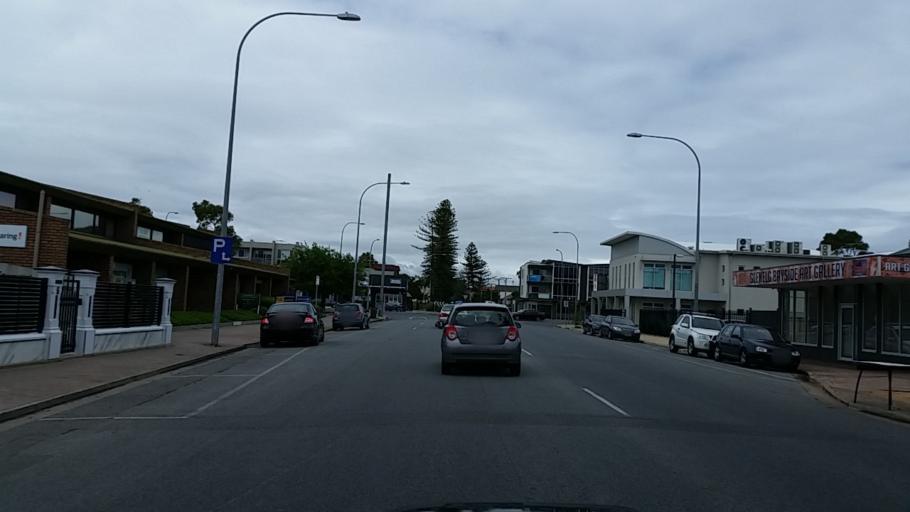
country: AU
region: South Australia
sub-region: Adelaide
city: Glenelg
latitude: -34.9755
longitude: 138.5174
